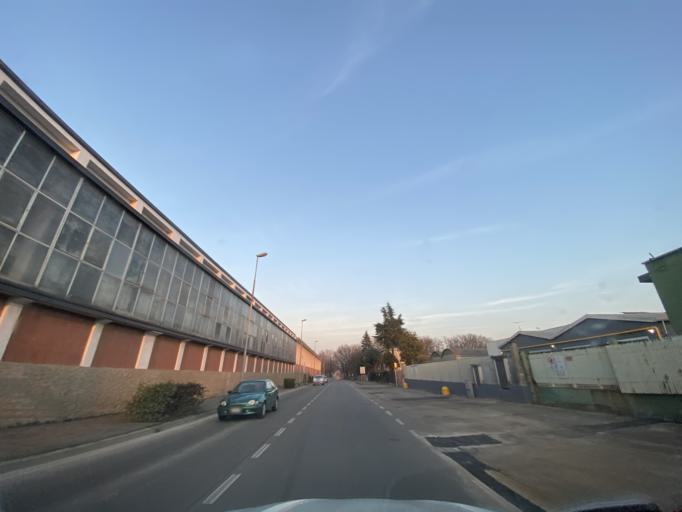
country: IT
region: Lombardy
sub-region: Provincia di Monza e Brianza
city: Villaggio del Sole
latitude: 45.6111
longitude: 9.0959
